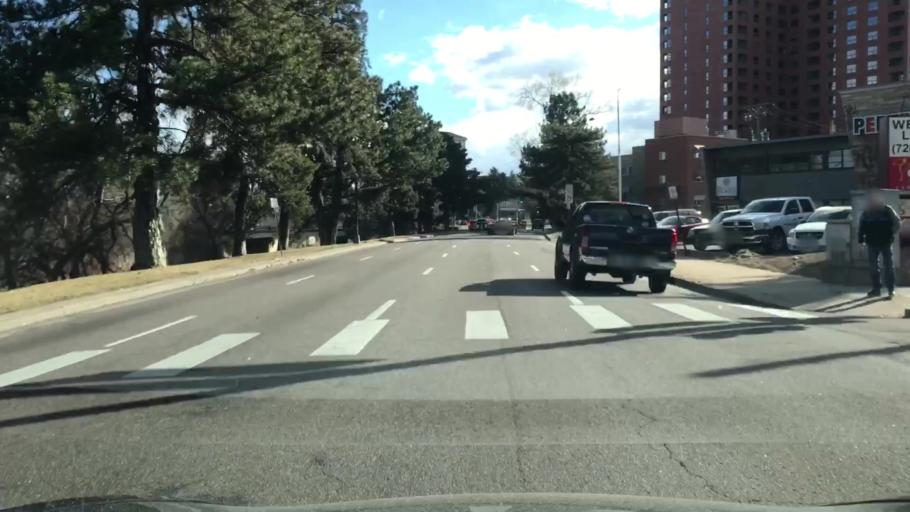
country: US
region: Colorado
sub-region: Denver County
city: Denver
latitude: 39.7204
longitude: -104.9792
